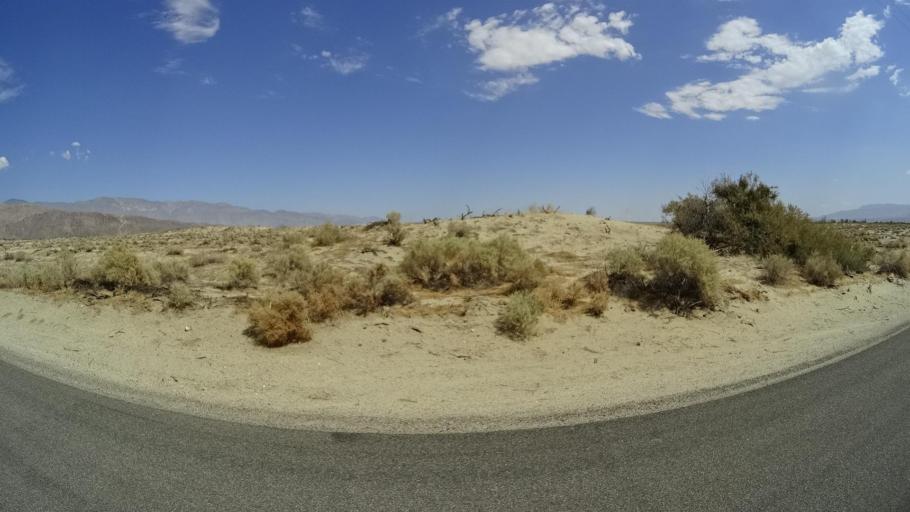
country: US
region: California
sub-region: San Diego County
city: Borrego Springs
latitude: 33.2771
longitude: -116.3487
